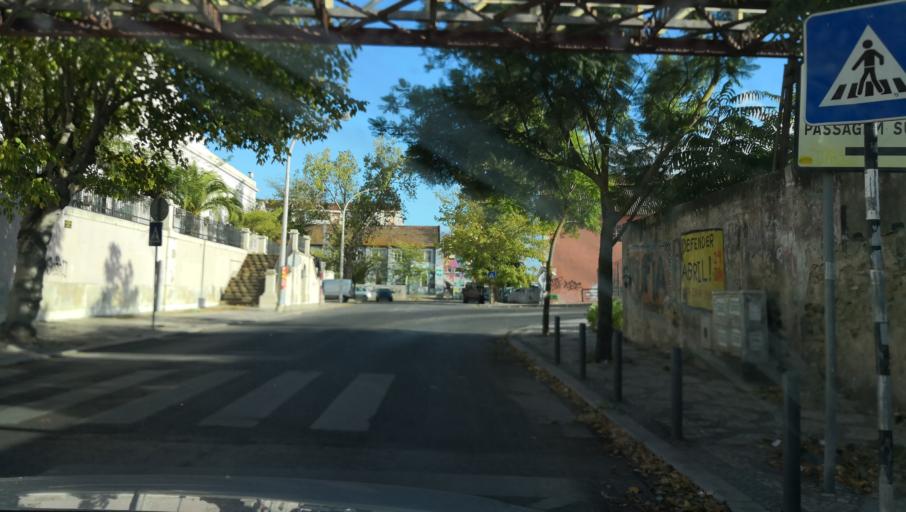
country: PT
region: Setubal
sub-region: Barreiro
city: Barreiro
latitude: 38.6568
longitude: -9.0787
